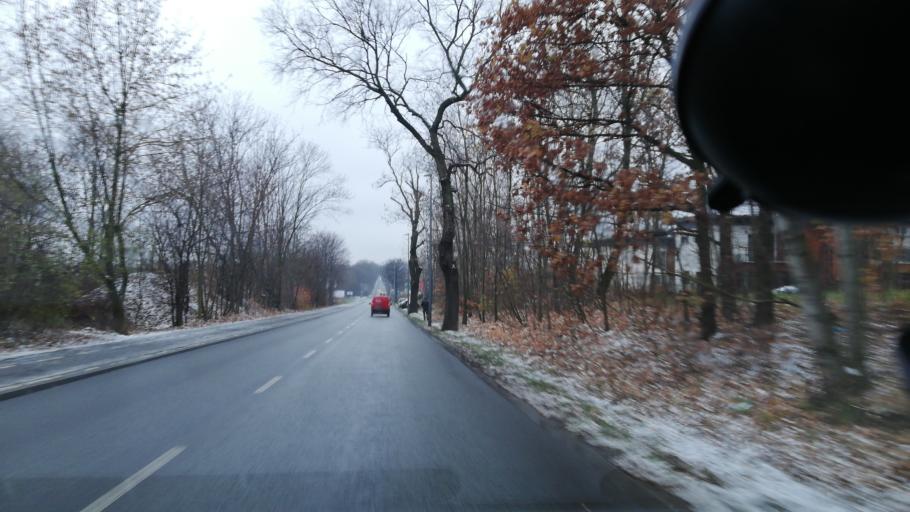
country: PL
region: Silesian Voivodeship
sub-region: Chorzow
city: Chorzow
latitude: 50.2978
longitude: 18.9949
